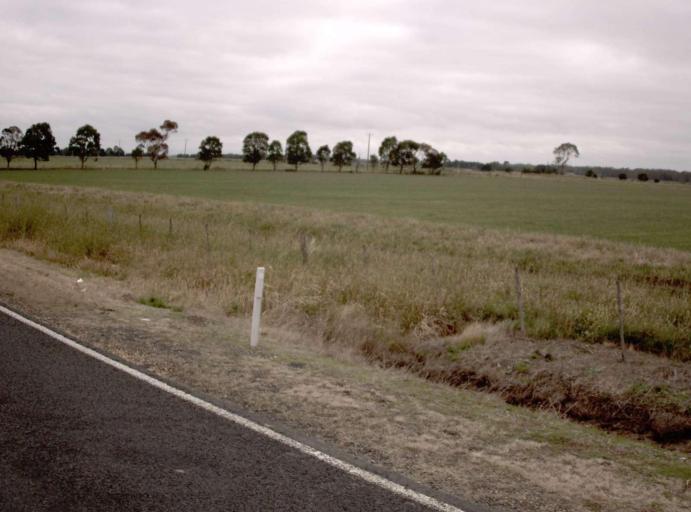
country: AU
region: Victoria
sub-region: Wellington
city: Sale
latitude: -38.0761
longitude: 146.9863
